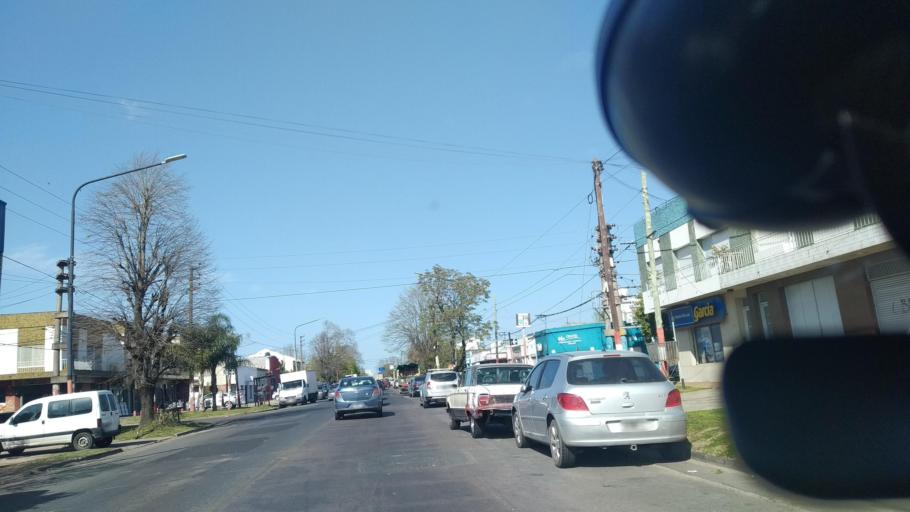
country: AR
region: Buenos Aires
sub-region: Partido de La Plata
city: La Plata
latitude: -34.9523
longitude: -57.9637
